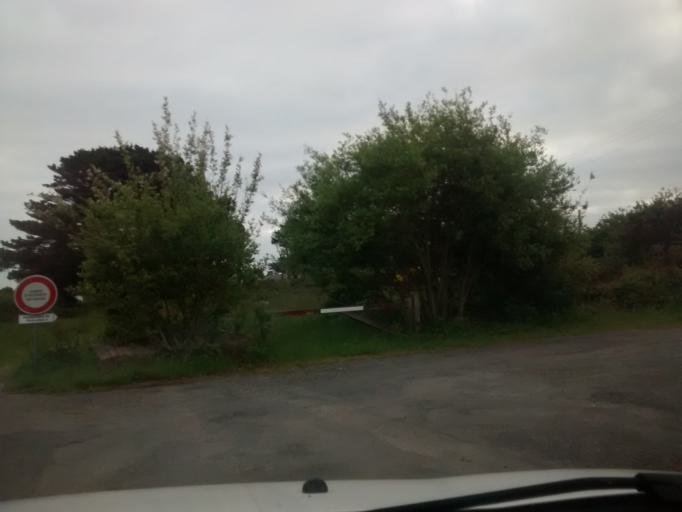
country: FR
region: Brittany
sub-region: Departement des Cotes-d'Armor
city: Tregastel
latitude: 48.8276
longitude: -3.4798
